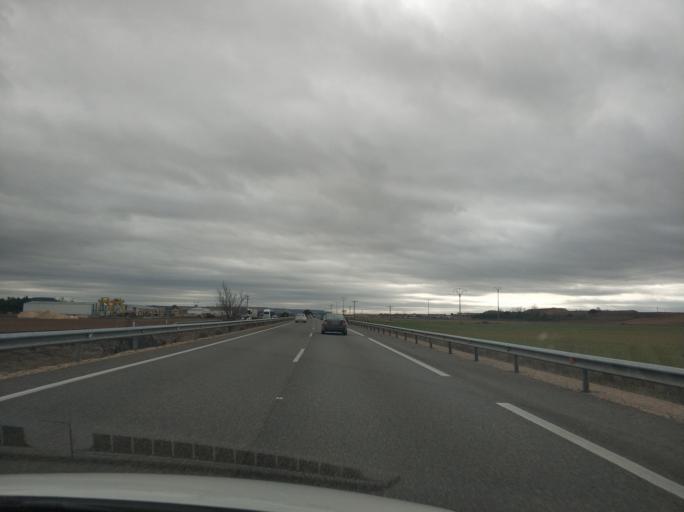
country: ES
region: Castille and Leon
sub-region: Provincia de Valladolid
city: Cubillas de Santa Marta
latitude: 41.8311
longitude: -4.5717
